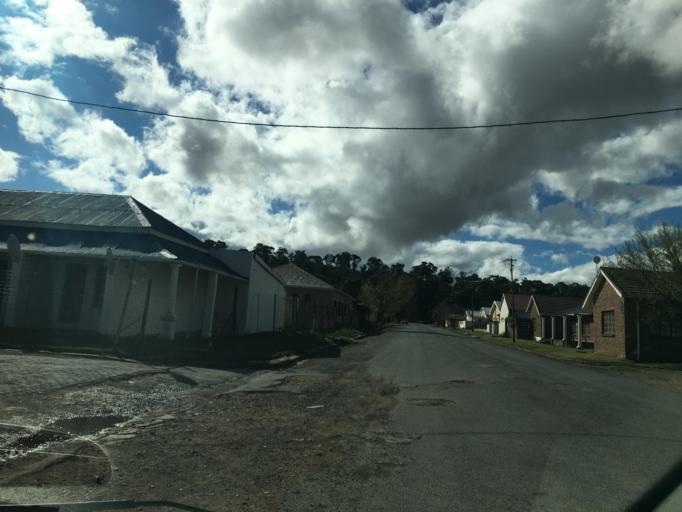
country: ZA
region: Eastern Cape
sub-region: Chris Hani District Municipality
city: Elliot
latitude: -31.3319
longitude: 27.8532
